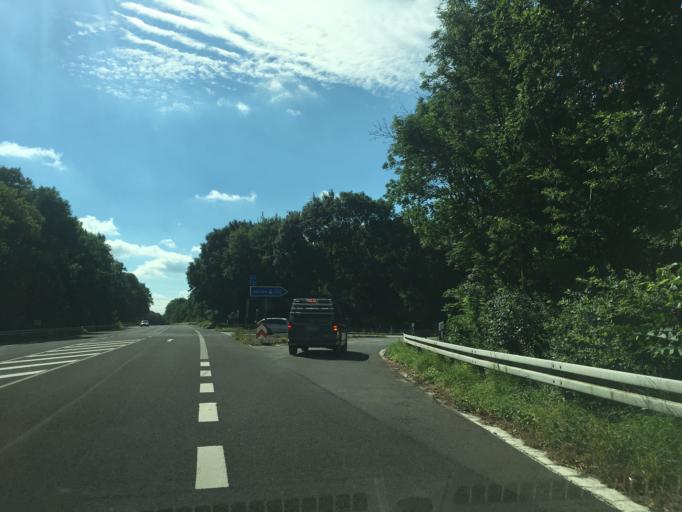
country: DE
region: North Rhine-Westphalia
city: Julich
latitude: 50.9664
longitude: 6.3621
